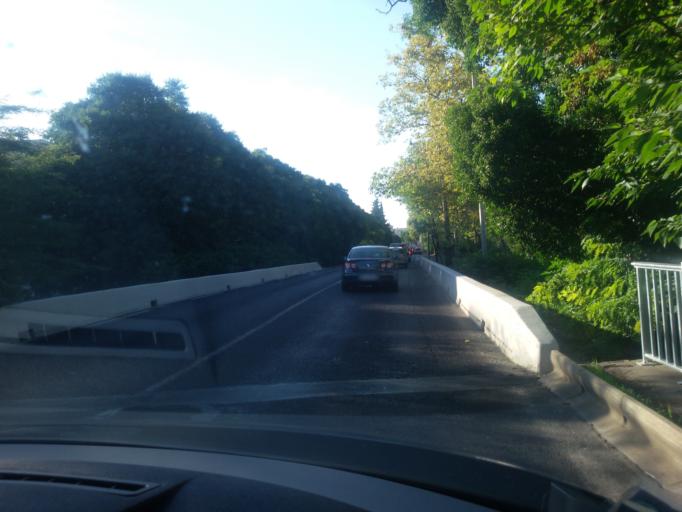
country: FR
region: Languedoc-Roussillon
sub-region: Departement de l'Herault
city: Montpellier
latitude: 43.6014
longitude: 3.8678
